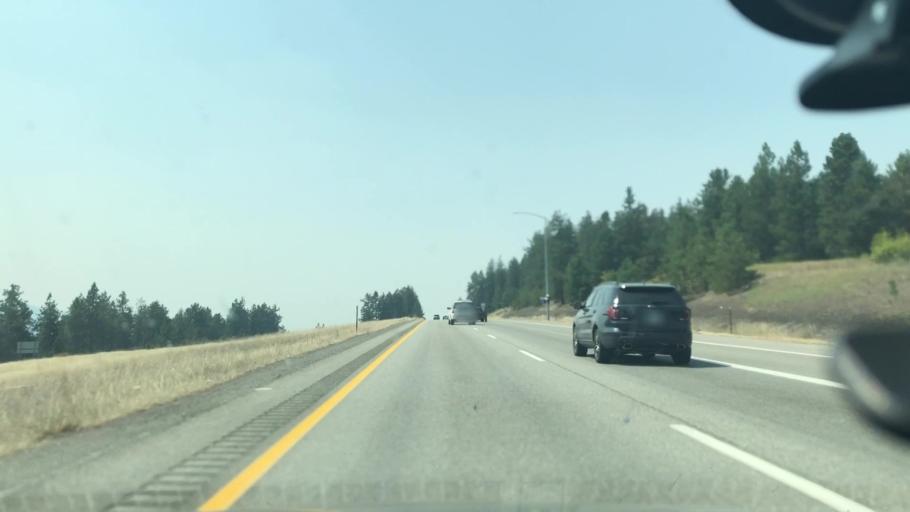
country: US
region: Idaho
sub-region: Kootenai County
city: Post Falls
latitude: 47.7093
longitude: -116.8750
